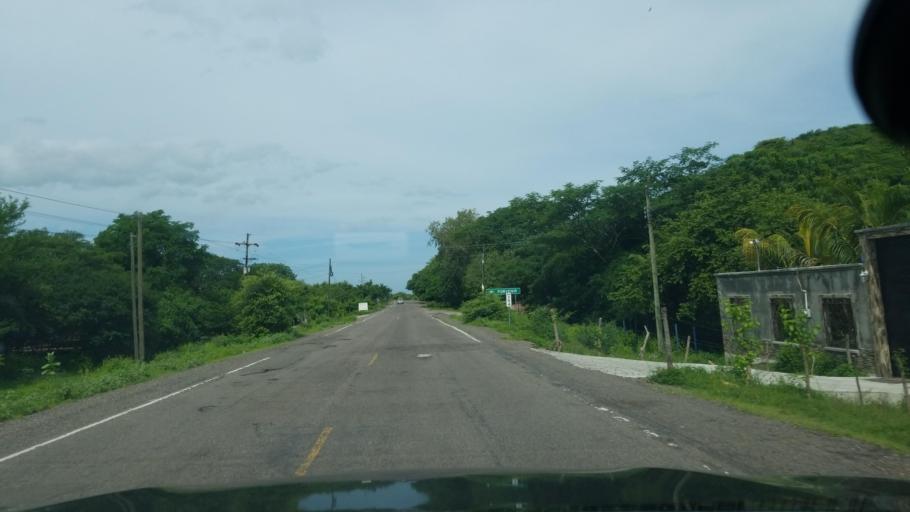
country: HN
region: Choluteca
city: Santa Ana de Yusguare
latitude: 13.3662
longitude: -87.0810
